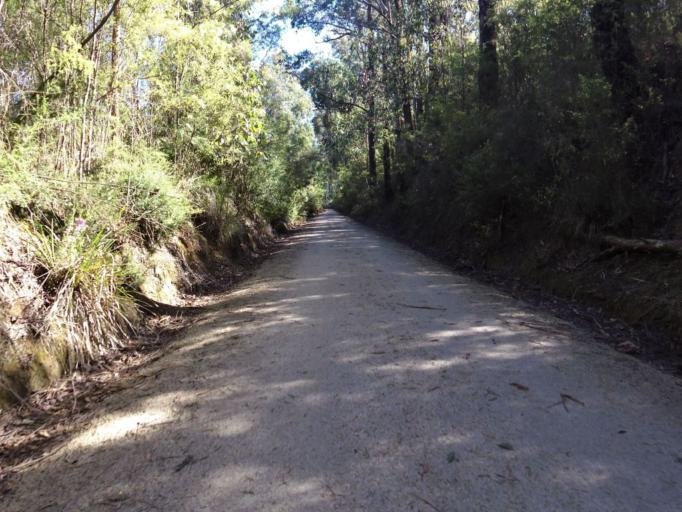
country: AU
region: Victoria
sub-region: Latrobe
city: Moe
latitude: -38.3895
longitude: 146.1850
